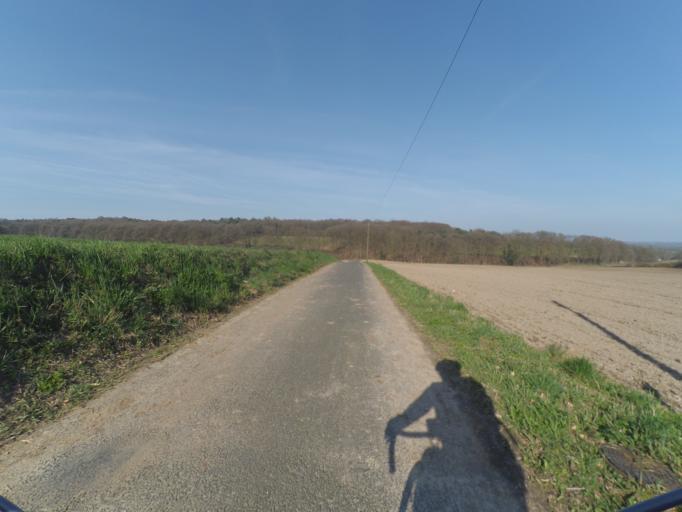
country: NL
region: Gelderland
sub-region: Gemeente Groesbeek
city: Berg en Dal
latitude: 51.8127
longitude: 5.9497
